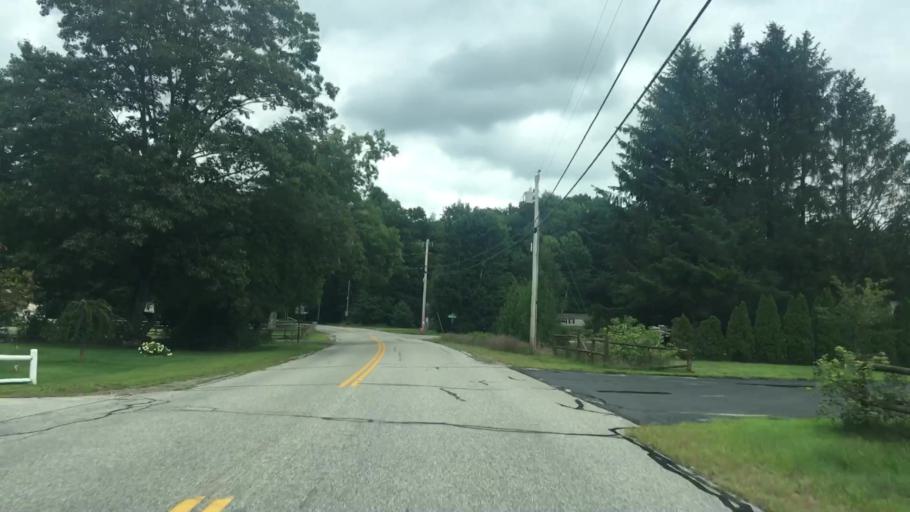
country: US
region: Maine
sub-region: York County
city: South Sanford
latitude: 43.4205
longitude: -70.6782
